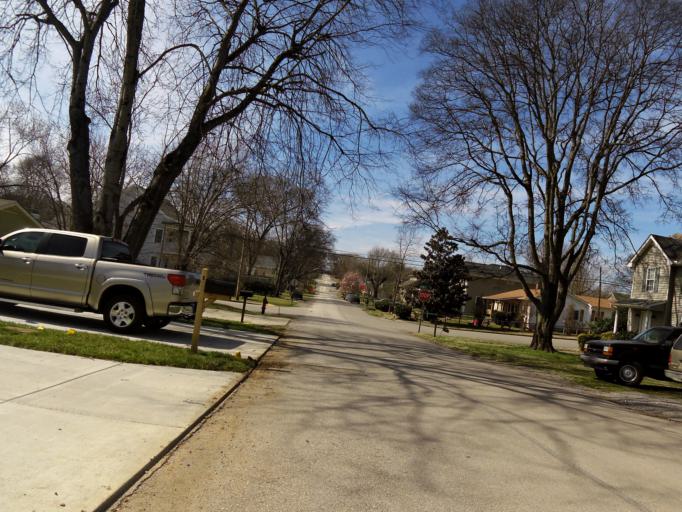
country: US
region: Tennessee
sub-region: Davidson County
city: Belle Meade
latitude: 36.1476
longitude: -86.8440
